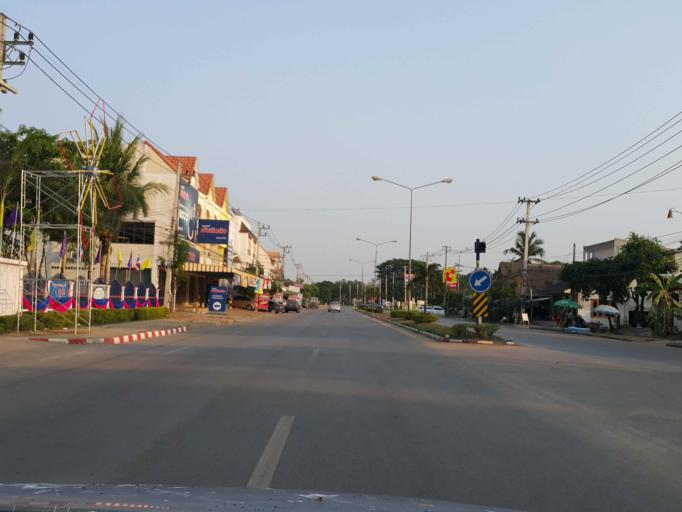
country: TH
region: Sukhothai
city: Sawankhalok
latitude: 17.2951
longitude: 99.8370
